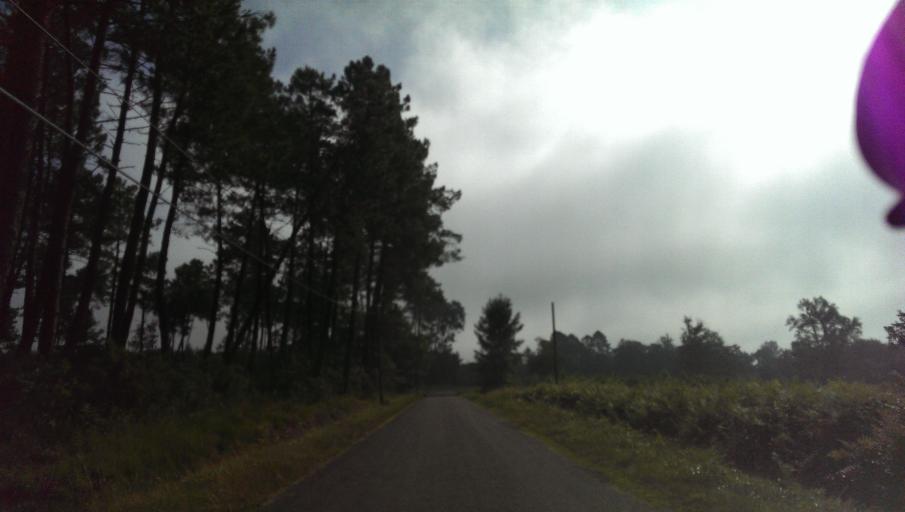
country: FR
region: Aquitaine
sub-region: Departement des Landes
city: Gabarret
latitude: 44.1082
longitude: -0.1183
